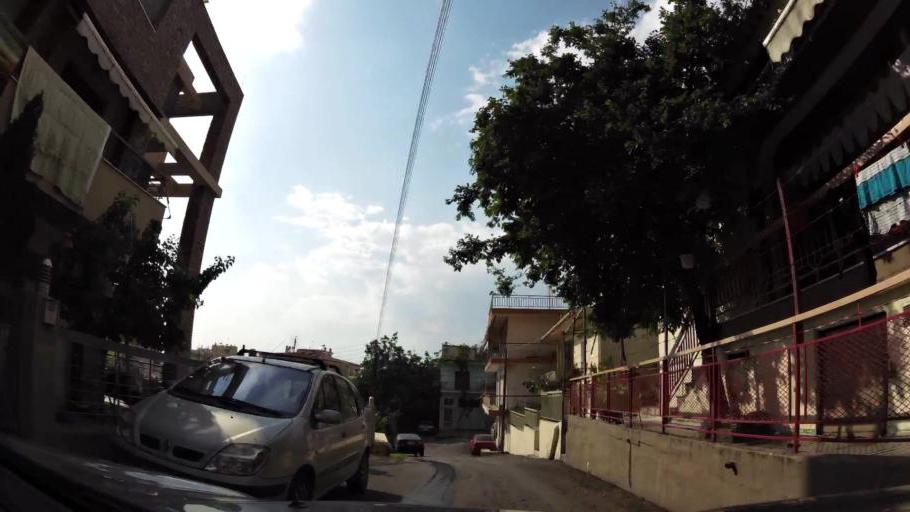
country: GR
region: Central Macedonia
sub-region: Nomos Thessalonikis
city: Sykies
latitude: 40.6589
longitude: 22.9601
